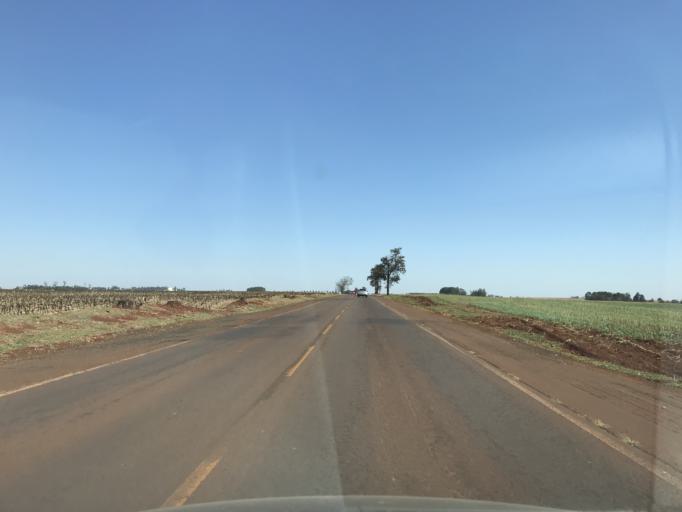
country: BR
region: Parana
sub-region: Palotina
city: Palotina
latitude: -24.3882
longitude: -53.8406
